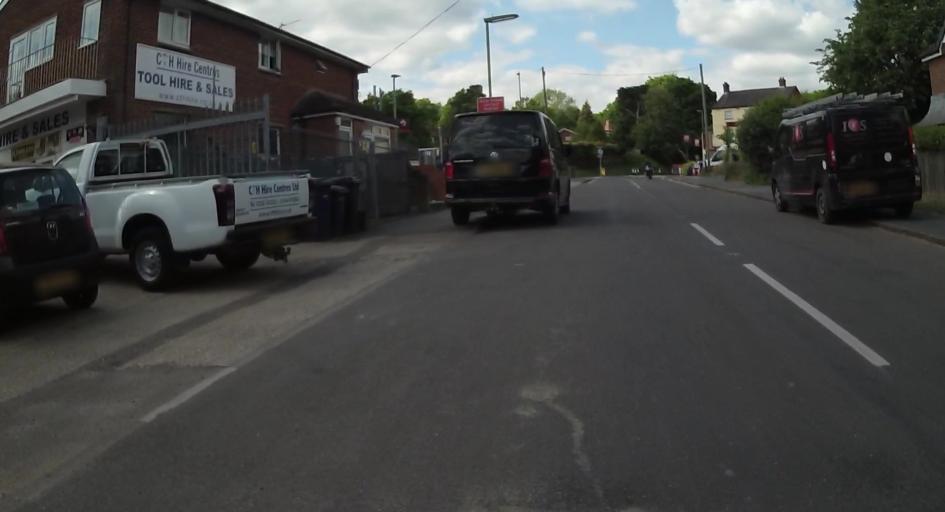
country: GB
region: England
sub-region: Surrey
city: Hale
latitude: 51.2389
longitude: -0.7858
